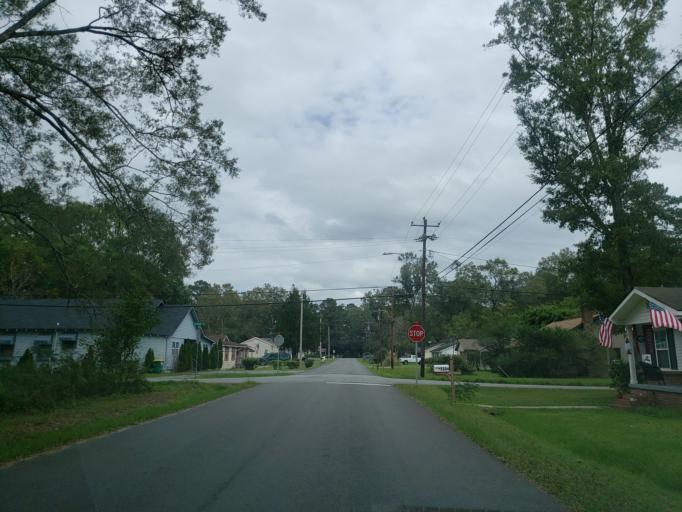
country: US
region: Georgia
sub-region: Chatham County
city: Pooler
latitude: 32.1168
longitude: -81.2430
